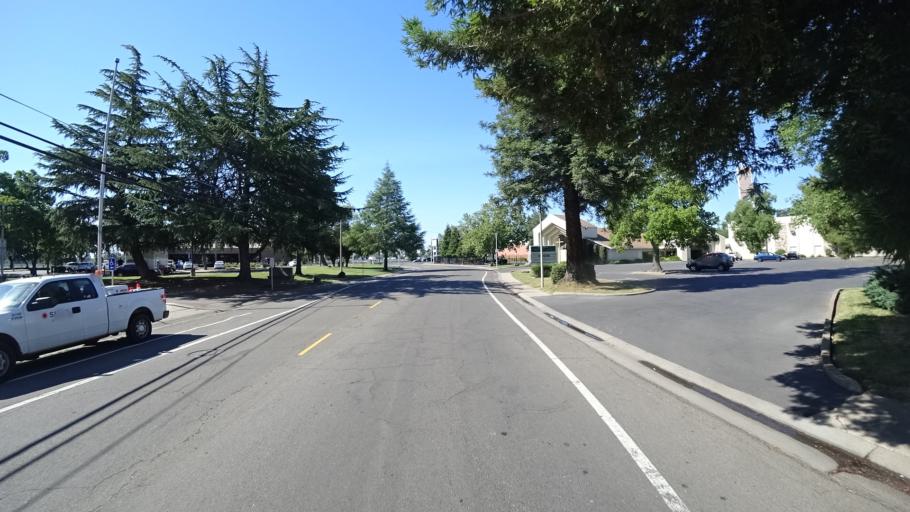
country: US
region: California
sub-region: Sacramento County
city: Rosemont
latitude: 38.5515
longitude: -121.3817
